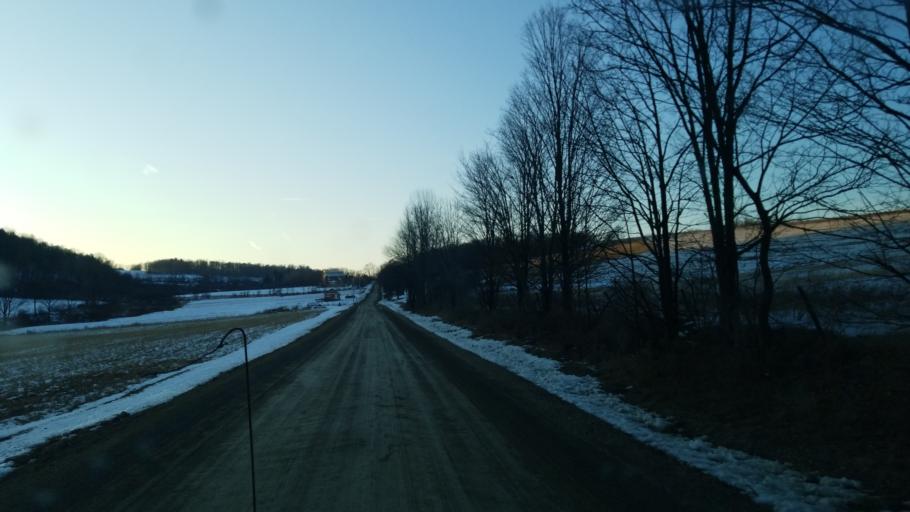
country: US
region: Pennsylvania
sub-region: Tioga County
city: Westfield
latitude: 42.0394
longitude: -77.5911
